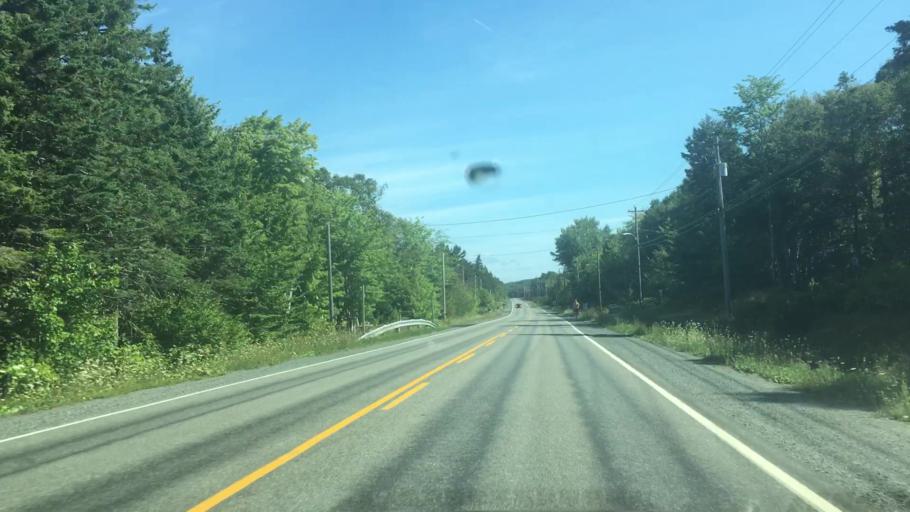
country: CA
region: Nova Scotia
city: Sydney
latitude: 45.9827
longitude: -60.4240
